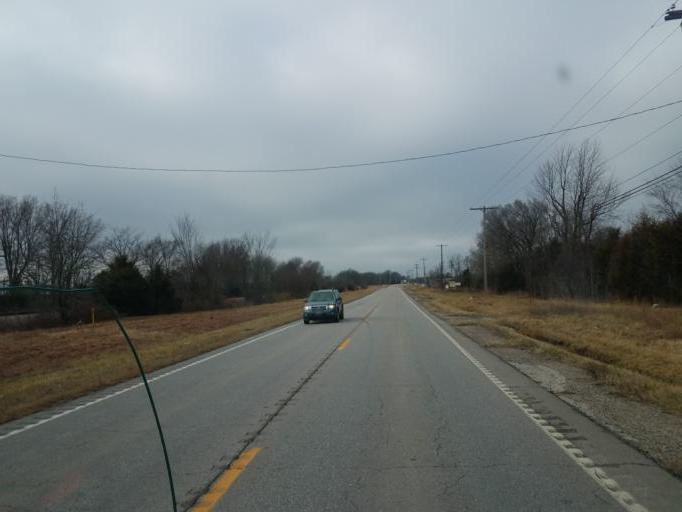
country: US
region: Missouri
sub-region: Greene County
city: Strafford
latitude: 37.2497
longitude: -93.1722
